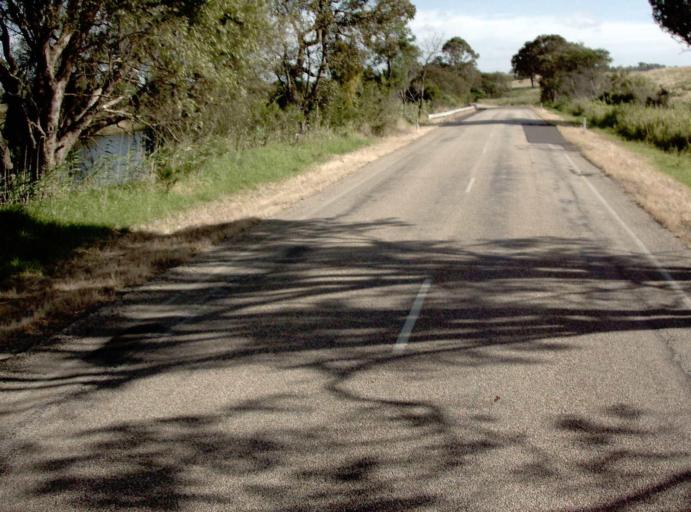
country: AU
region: Victoria
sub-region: East Gippsland
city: Lakes Entrance
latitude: -37.8352
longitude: 147.8619
